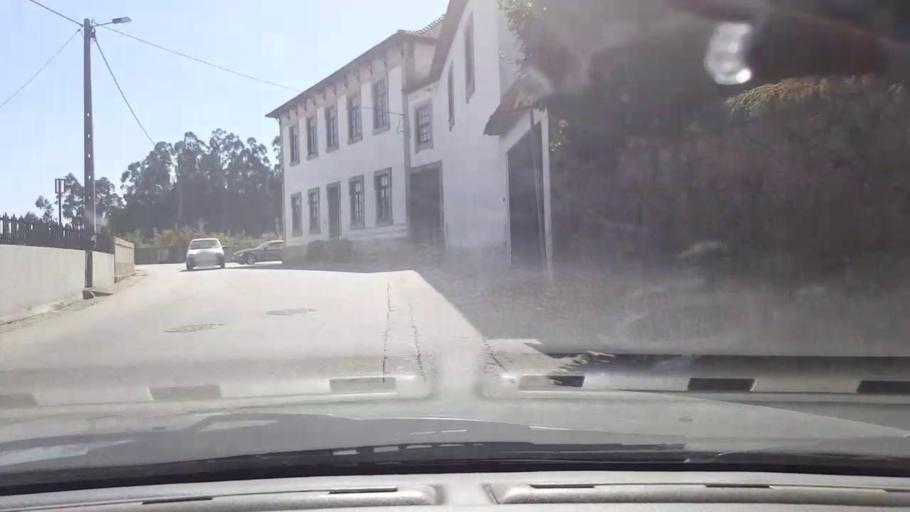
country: PT
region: Porto
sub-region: Matosinhos
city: Lavra
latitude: 41.2633
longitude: -8.6902
